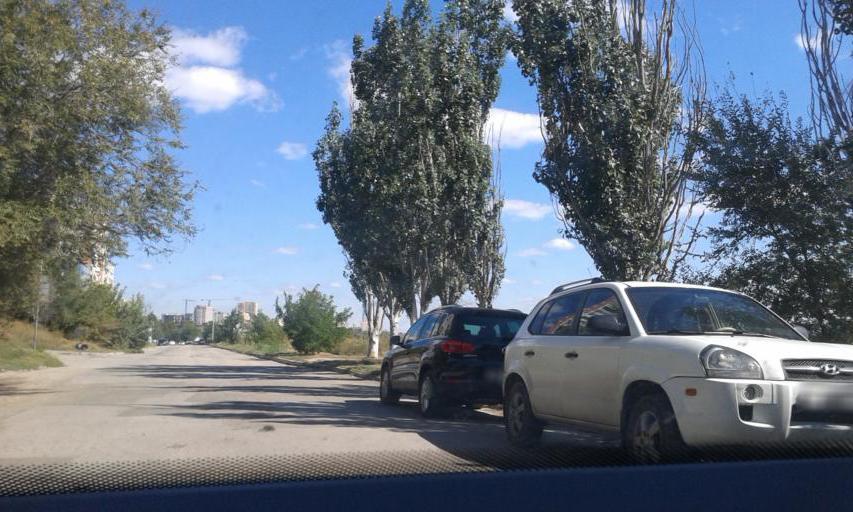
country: RU
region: Volgograd
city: Volgograd
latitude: 48.6740
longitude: 44.4770
